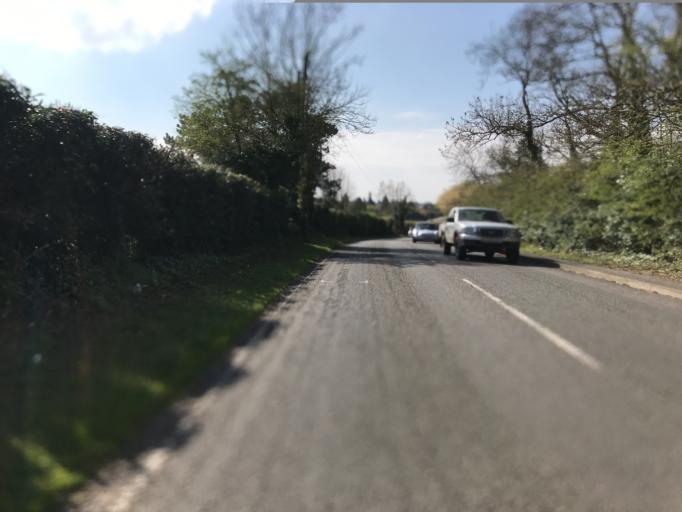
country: GB
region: England
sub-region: Cambridgeshire
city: Sawston
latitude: 52.1576
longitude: 0.1542
